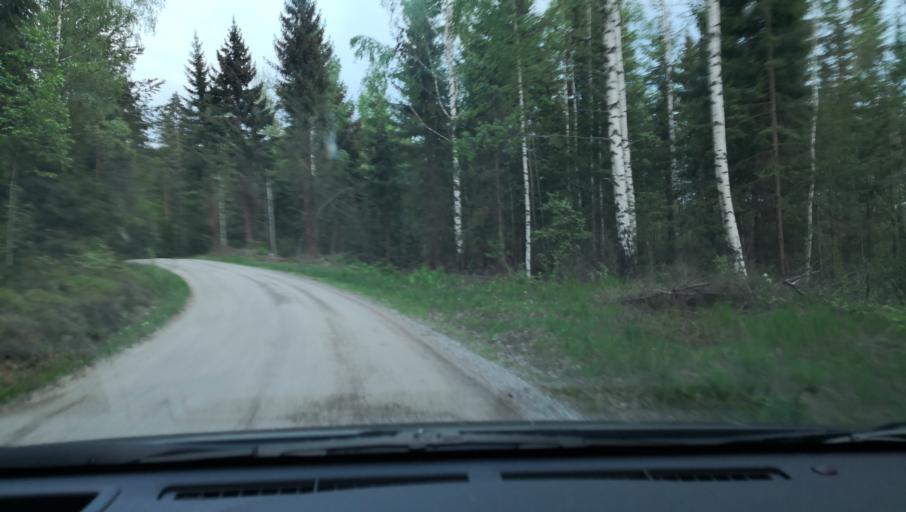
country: SE
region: Vaestmanland
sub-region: Skinnskattebergs Kommun
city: Skinnskatteberg
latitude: 59.7350
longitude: 15.4713
